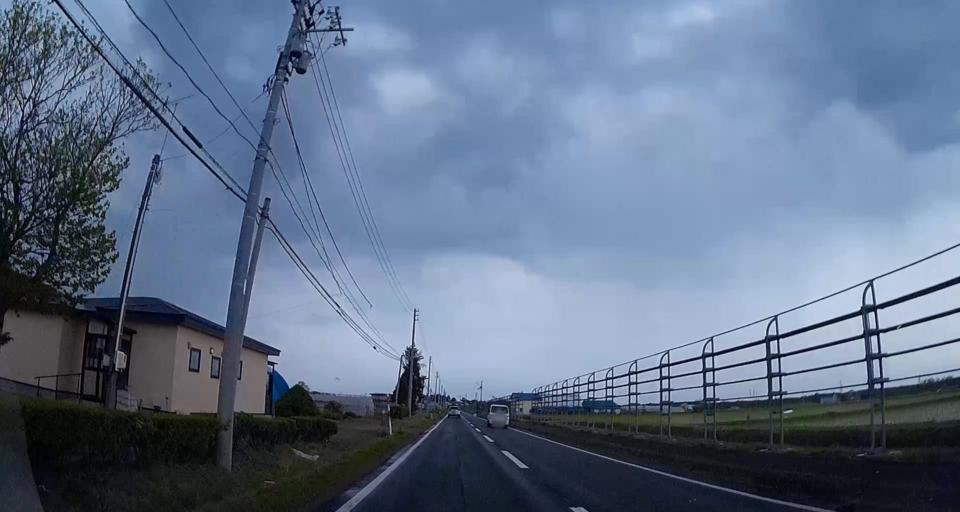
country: JP
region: Hokkaido
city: Chitose
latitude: 42.7020
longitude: 141.8500
